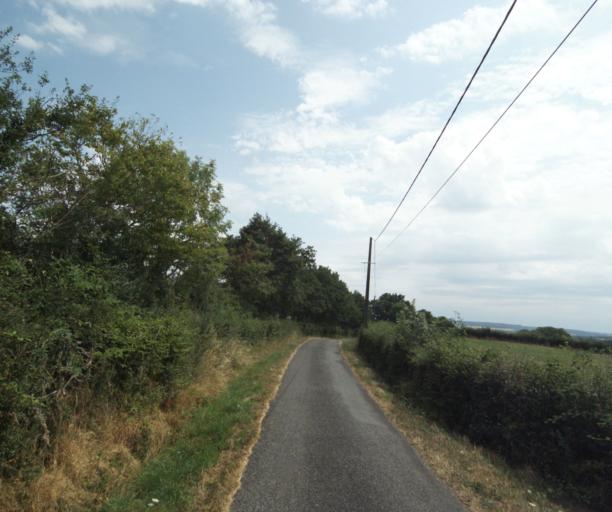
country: FR
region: Bourgogne
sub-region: Departement de Saone-et-Loire
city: Gueugnon
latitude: 46.6038
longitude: 4.0370
